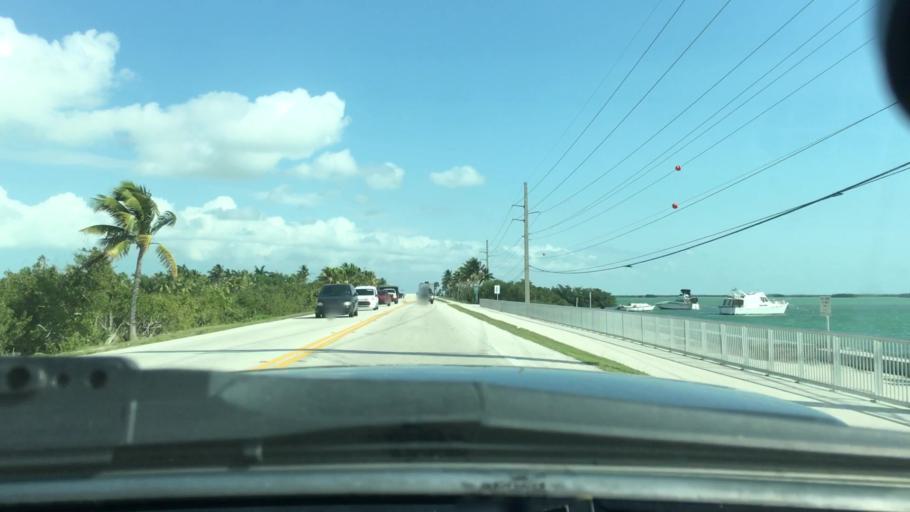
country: US
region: Florida
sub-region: Monroe County
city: Big Coppitt Key
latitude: 24.6013
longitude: -81.6476
